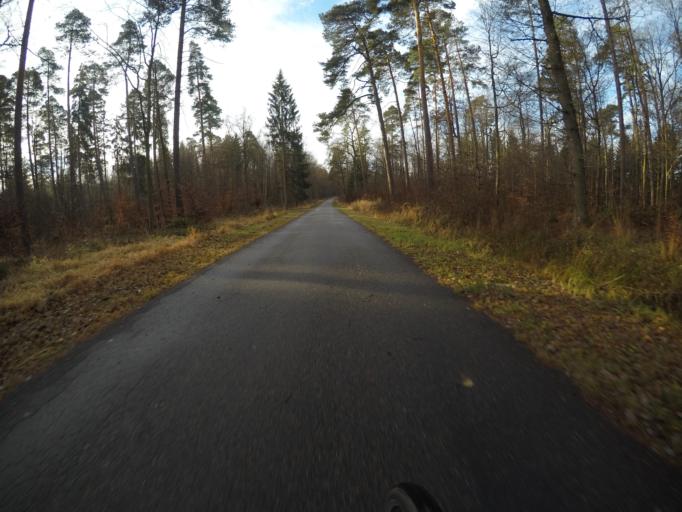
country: DE
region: Baden-Wuerttemberg
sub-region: Regierungsbezirk Stuttgart
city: Sindelfingen
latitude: 48.7259
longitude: 9.0490
